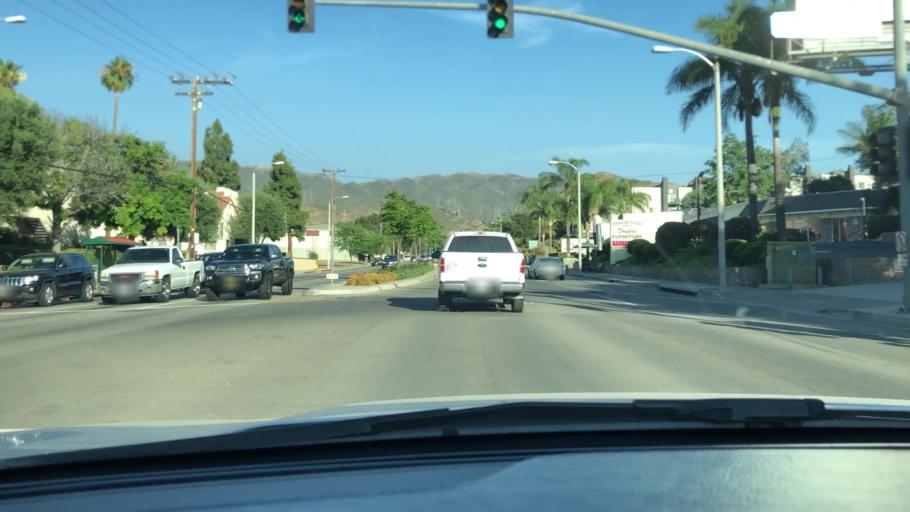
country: US
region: California
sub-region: Los Angeles County
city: Santa Clarita
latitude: 34.3709
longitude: -118.5148
